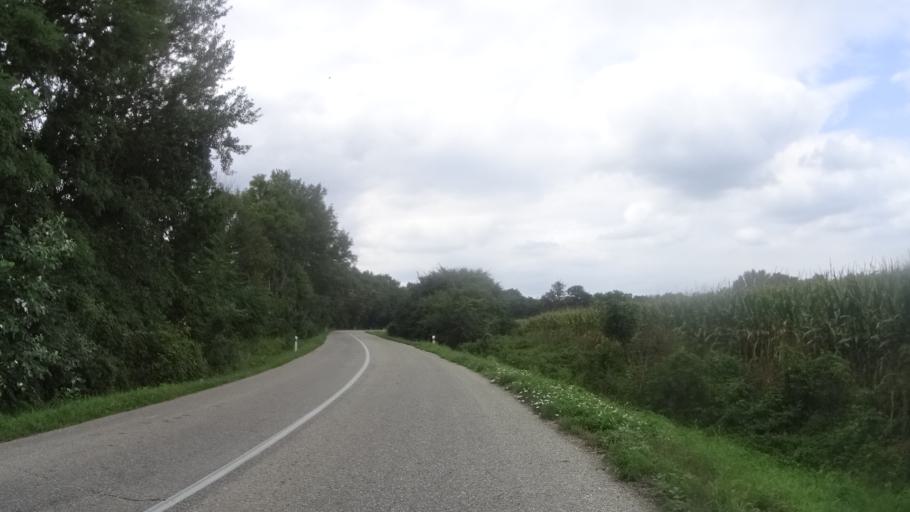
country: SK
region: Trnavsky
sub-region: Okres Dunajska Streda
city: Velky Meder
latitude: 47.7546
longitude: 17.7971
